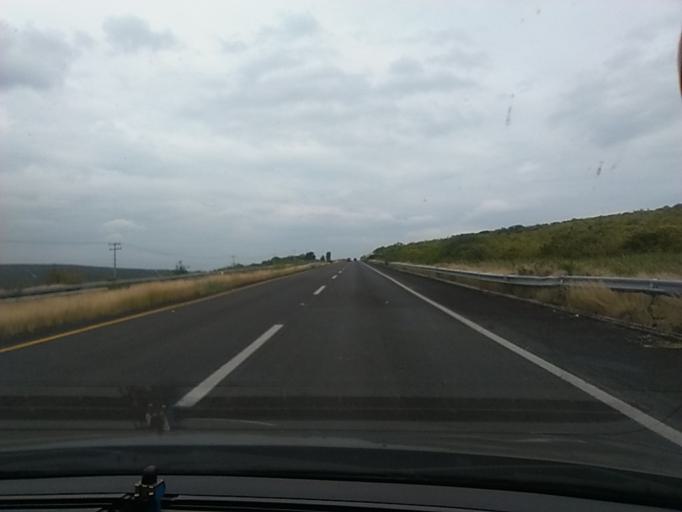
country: MX
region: Michoacan
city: Ecuandureo
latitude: 20.1724
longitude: -102.1571
